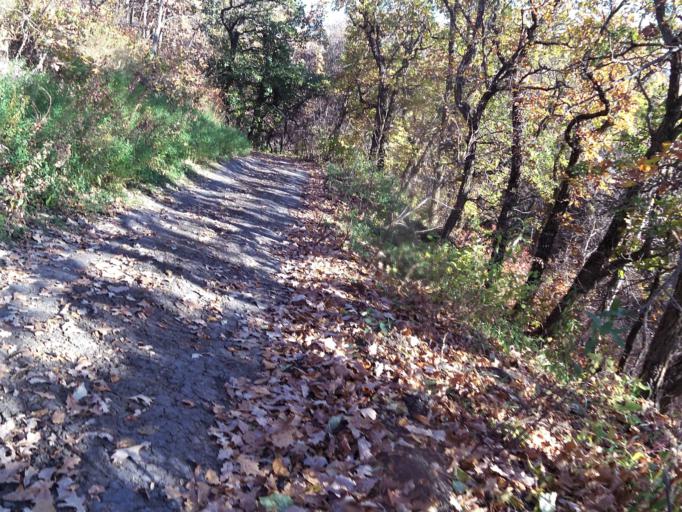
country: CA
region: Manitoba
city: Morden
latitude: 48.9414
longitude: -98.0635
